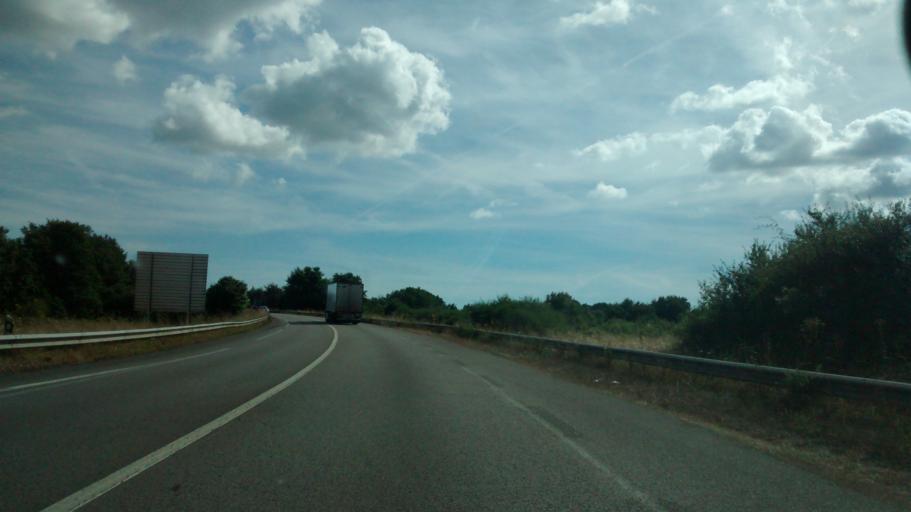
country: FR
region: Pays de la Loire
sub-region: Departement de la Loire-Atlantique
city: Bouguenais
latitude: 47.1705
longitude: -1.5943
